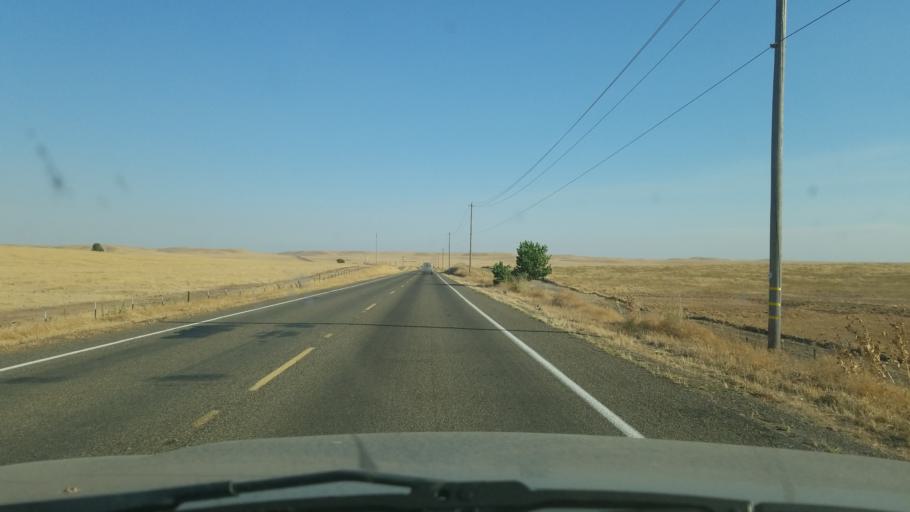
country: US
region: California
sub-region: Merced County
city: Merced
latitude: 37.4850
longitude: -120.4461
